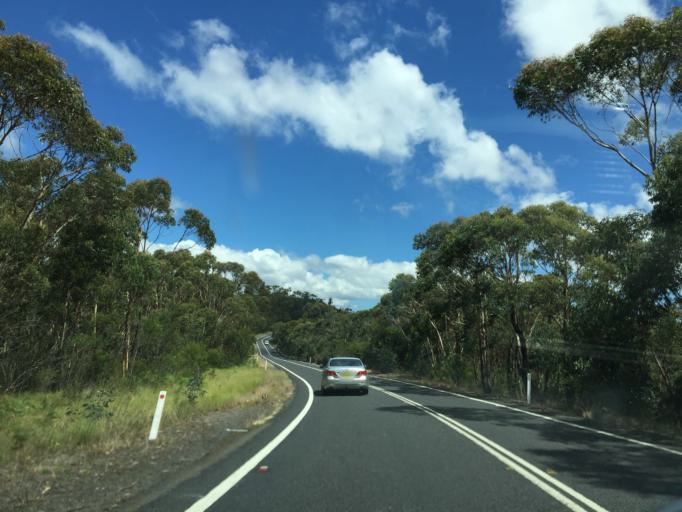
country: AU
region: New South Wales
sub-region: Blue Mountains Municipality
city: Blackheath
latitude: -33.5563
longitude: 150.3749
